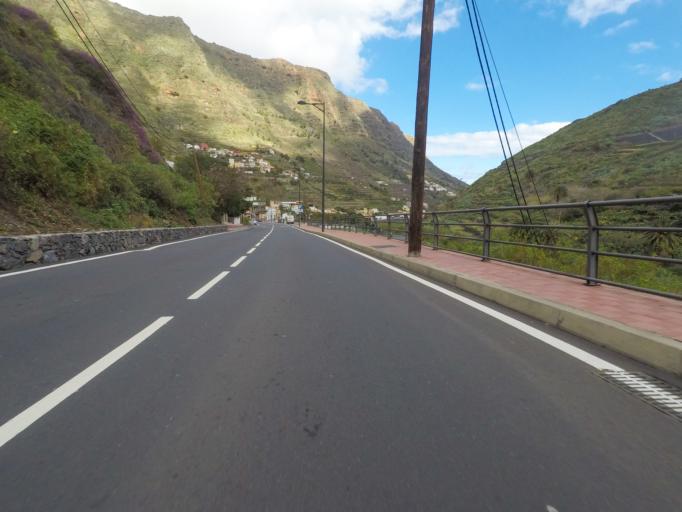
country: ES
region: Canary Islands
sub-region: Provincia de Santa Cruz de Tenerife
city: Hermigua
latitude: 28.1614
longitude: -17.1981
